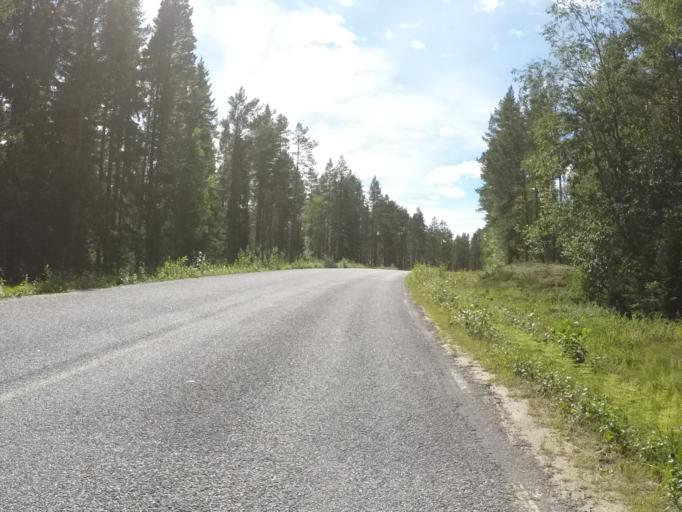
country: SE
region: Vaesterbotten
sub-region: Robertsfors Kommun
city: Robertsfors
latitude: 63.9595
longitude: 20.8074
